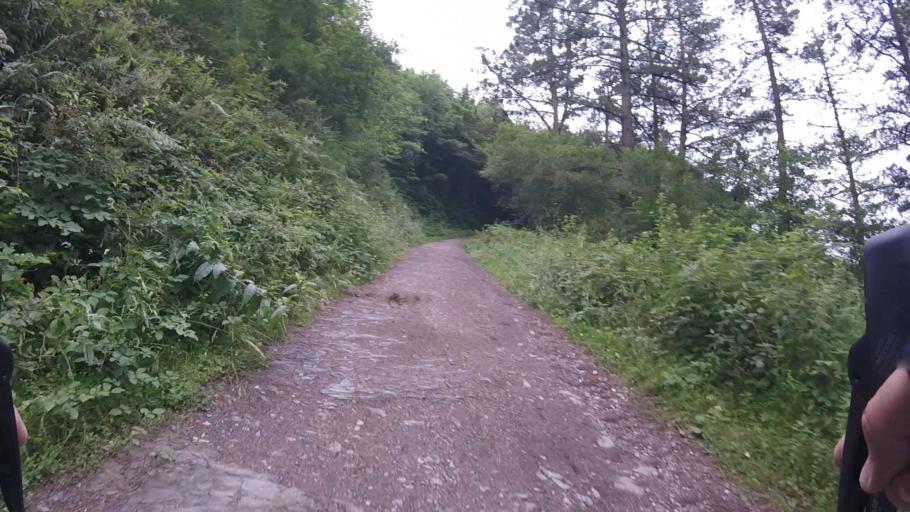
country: ES
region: Navarre
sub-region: Provincia de Navarra
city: Arano
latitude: 43.2537
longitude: -1.8891
